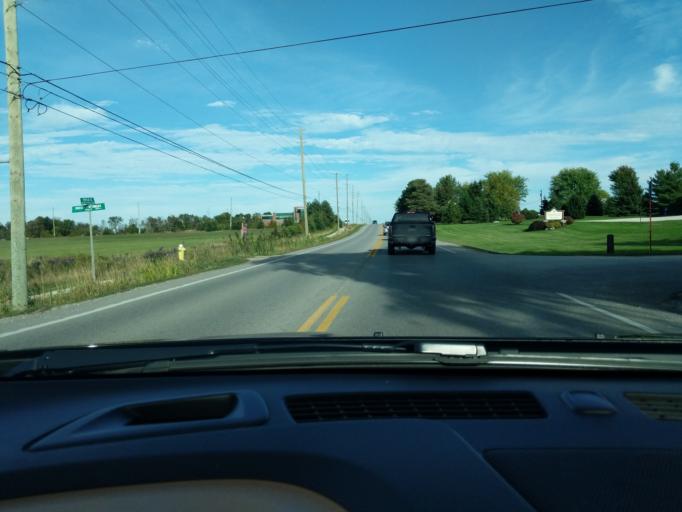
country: CA
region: Ontario
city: Collingwood
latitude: 44.4825
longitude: -80.1957
